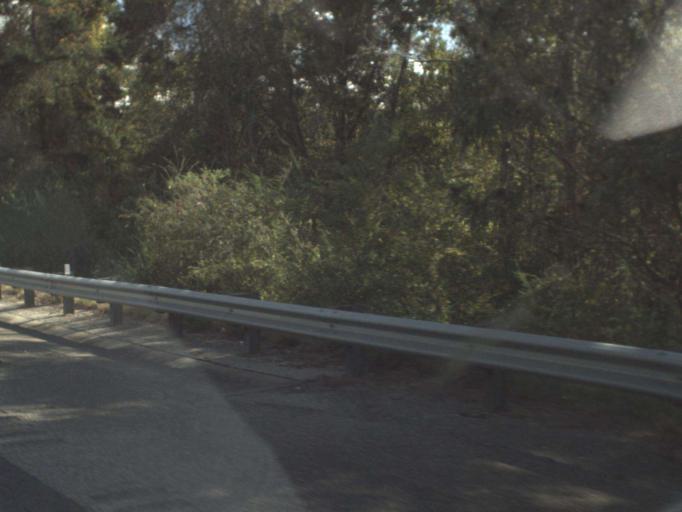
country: US
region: Florida
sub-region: Gadsden County
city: Quincy
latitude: 30.5576
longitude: -84.6376
